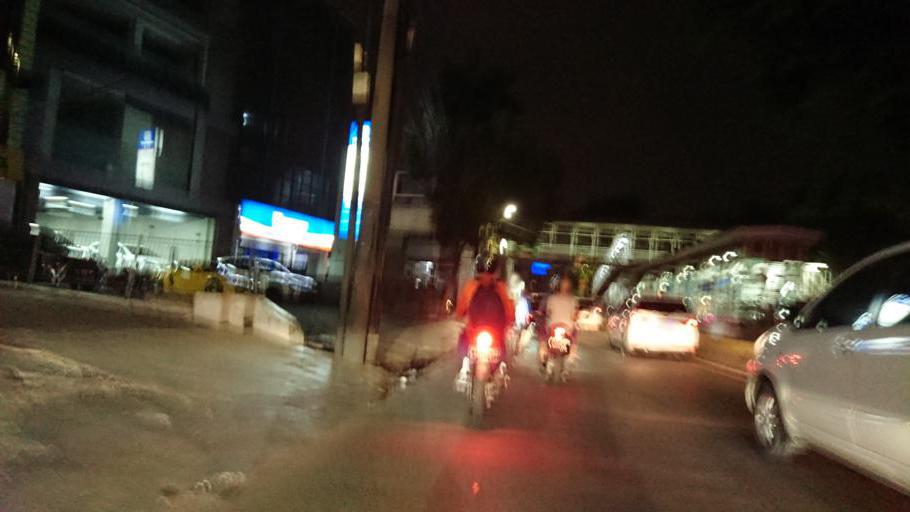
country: ID
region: Banten
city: South Tangerang
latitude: -6.2523
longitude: 106.7817
